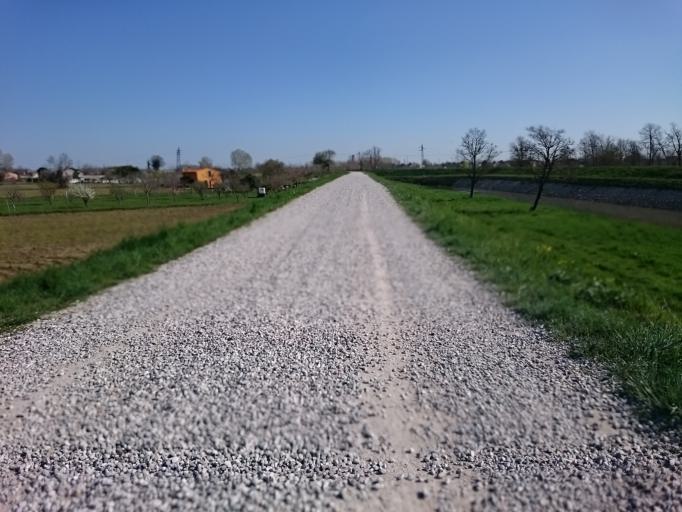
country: IT
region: Veneto
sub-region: Provincia di Padova
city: Ponte San Nicolo
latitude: 45.3788
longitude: 11.9239
